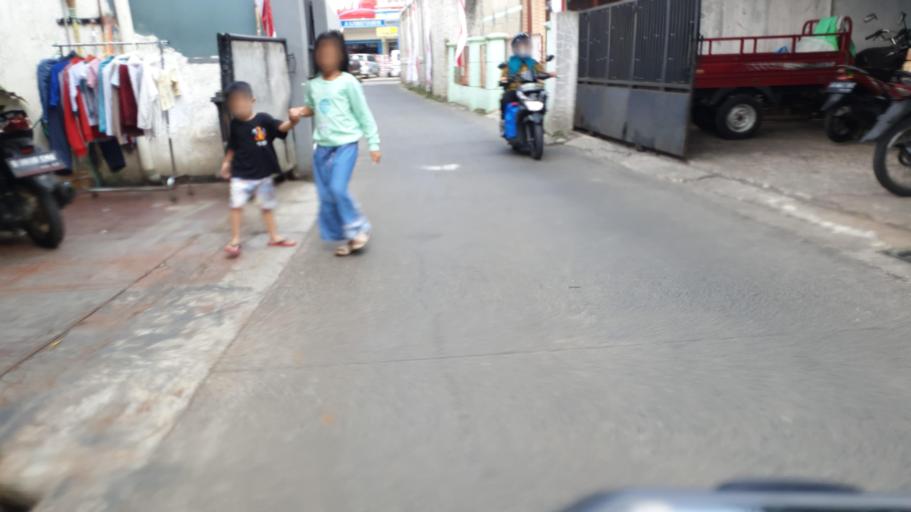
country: ID
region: West Java
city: Depok
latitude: -6.3718
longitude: 106.8515
